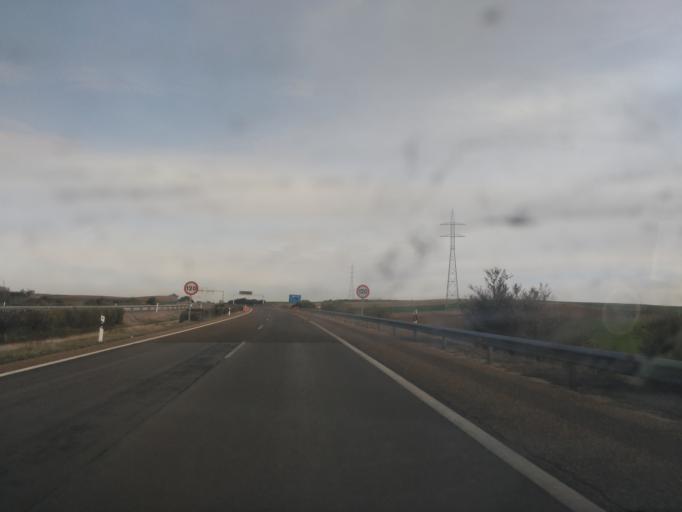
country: ES
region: Castille and Leon
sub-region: Provincia de Salamanca
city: Cabrerizos
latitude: 41.0009
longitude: -5.6185
